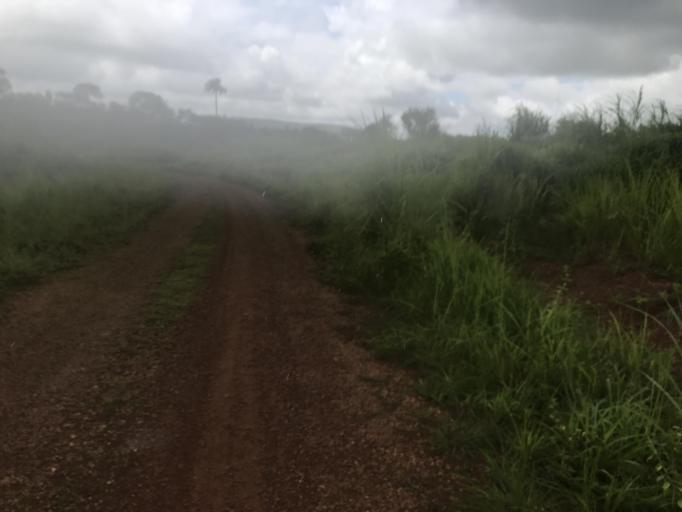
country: GN
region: Nzerekore
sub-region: Prefecture de Guekedou
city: Gueckedou
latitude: 8.4746
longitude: -10.2884
